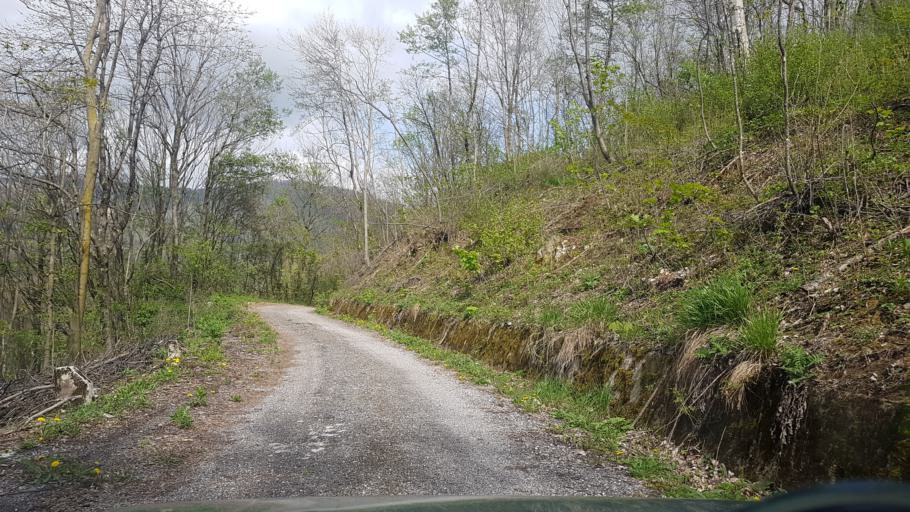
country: IT
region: Friuli Venezia Giulia
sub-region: Provincia di Udine
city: Attimis
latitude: 46.2117
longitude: 13.3386
